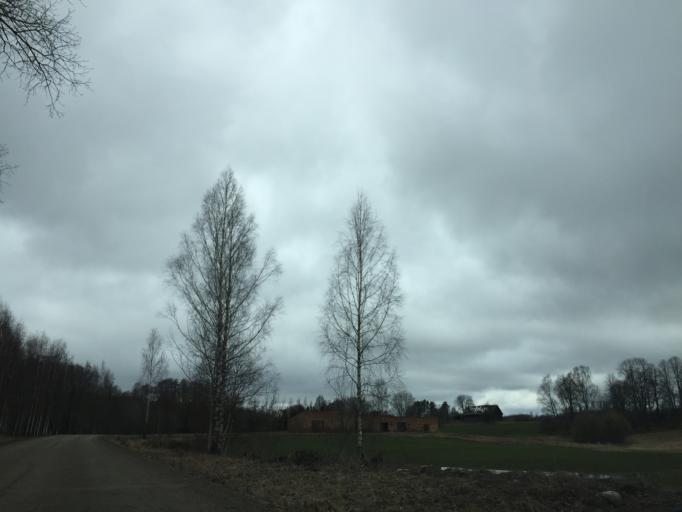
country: LV
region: Ilukste
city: Ilukste
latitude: 56.0283
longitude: 26.2194
